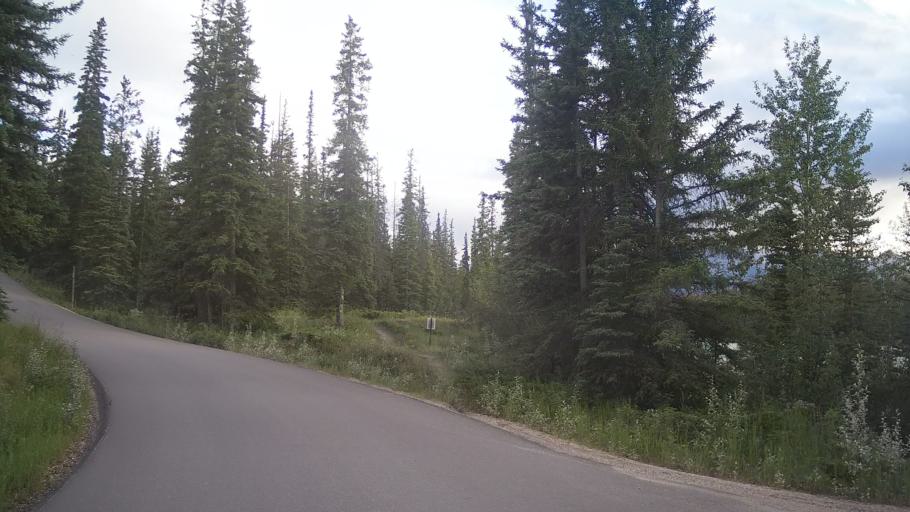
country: CA
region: Alberta
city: Jasper Park Lodge
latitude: 52.9324
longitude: -118.0331
